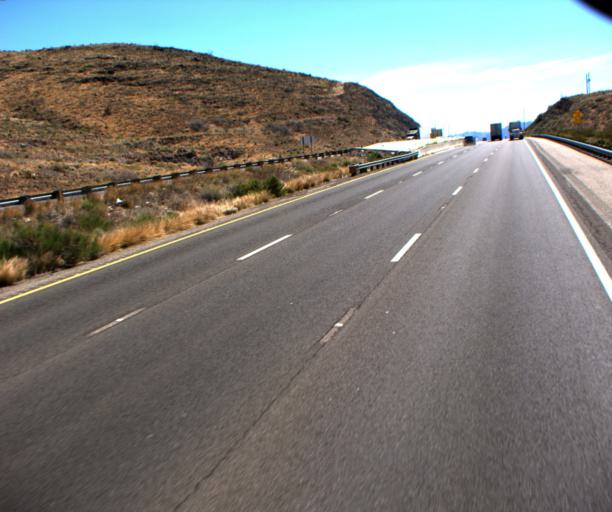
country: US
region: Arizona
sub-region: Mohave County
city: Kingman
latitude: 35.2099
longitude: -114.1062
